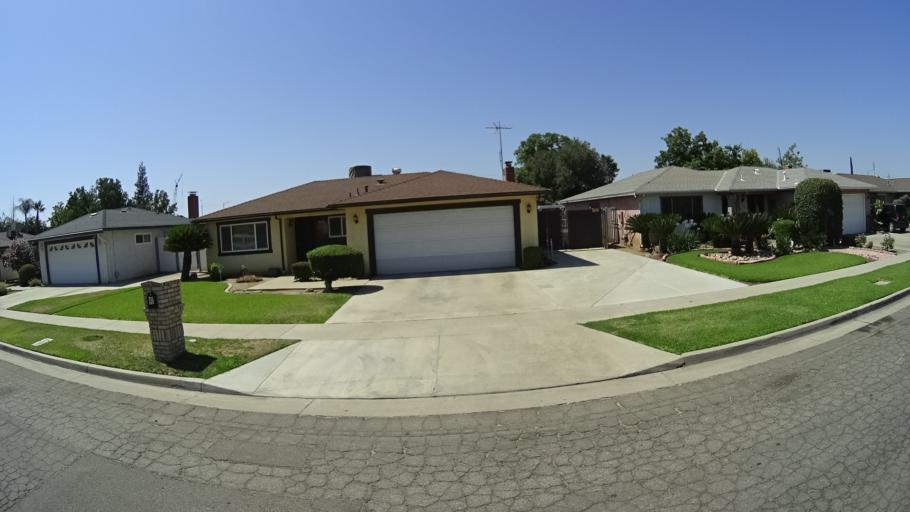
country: US
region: California
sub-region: Fresno County
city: West Park
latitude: 36.7149
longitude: -119.8056
